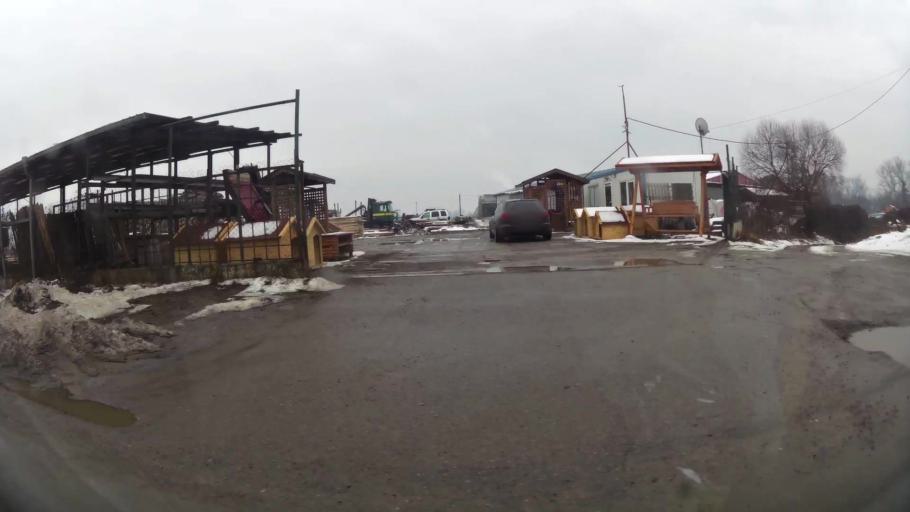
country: BG
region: Sofiya
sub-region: Obshtina Bozhurishte
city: Bozhurishte
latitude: 42.6918
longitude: 23.2303
